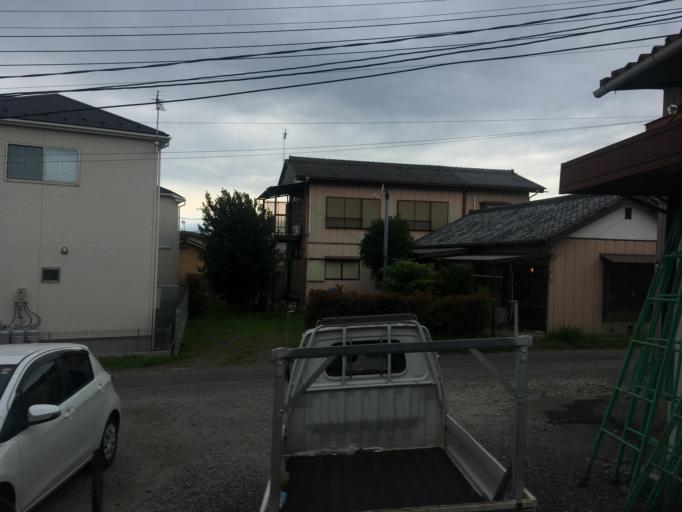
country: JP
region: Gunma
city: Maebashi-shi
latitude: 36.3962
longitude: 139.1164
